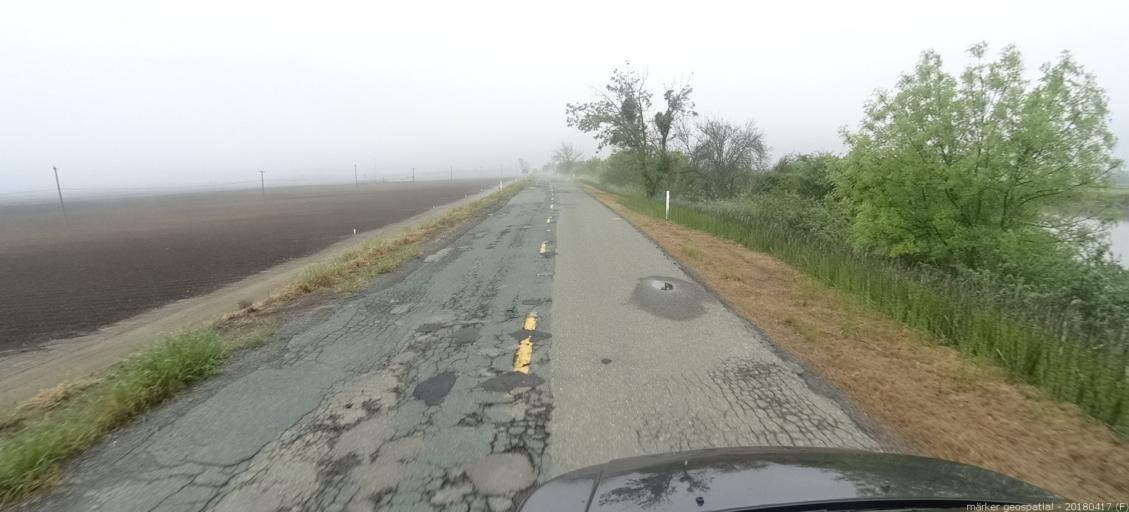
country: US
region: California
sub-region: Sacramento County
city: Walnut Grove
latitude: 38.1845
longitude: -121.5652
